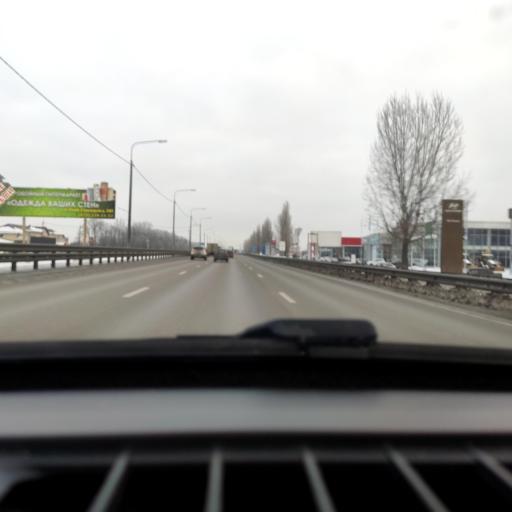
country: RU
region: Voronezj
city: Podgornoye
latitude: 51.7752
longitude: 39.1952
